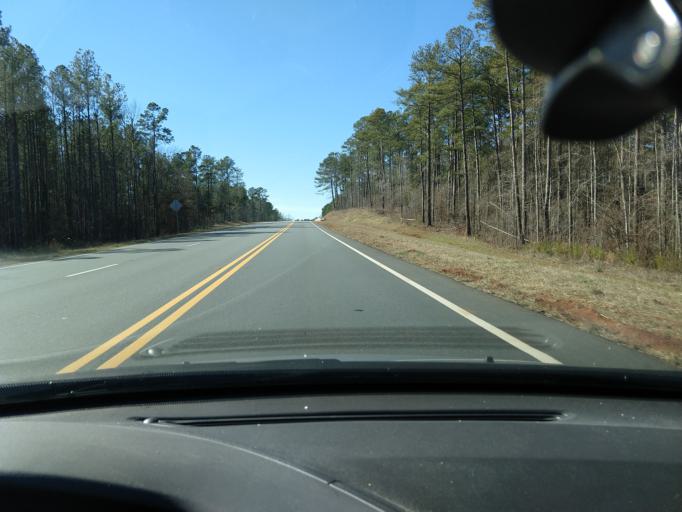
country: US
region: Georgia
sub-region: Jasper County
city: Monticello
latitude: 33.2110
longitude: -83.7588
